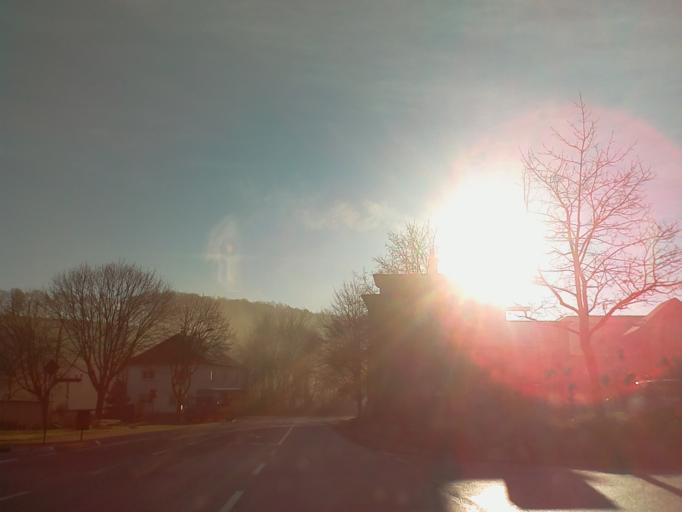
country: DE
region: Hesse
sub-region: Regierungsbezirk Darmstadt
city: Erbach
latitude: 49.6744
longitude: 8.9237
